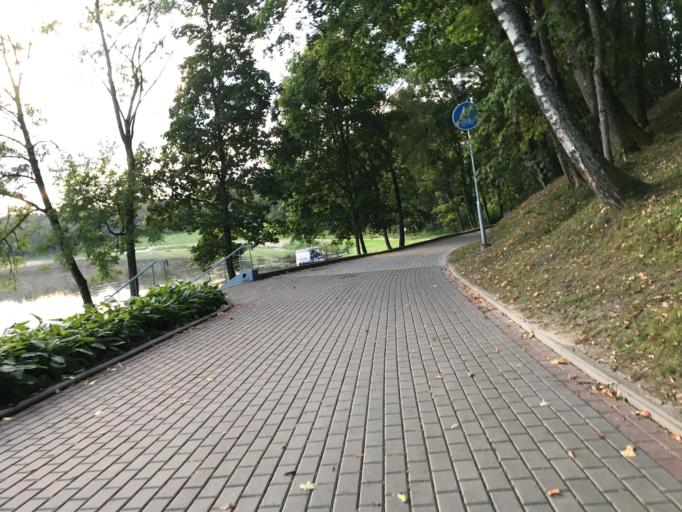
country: LT
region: Alytaus apskritis
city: Druskininkai
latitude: 54.0198
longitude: 23.9794
